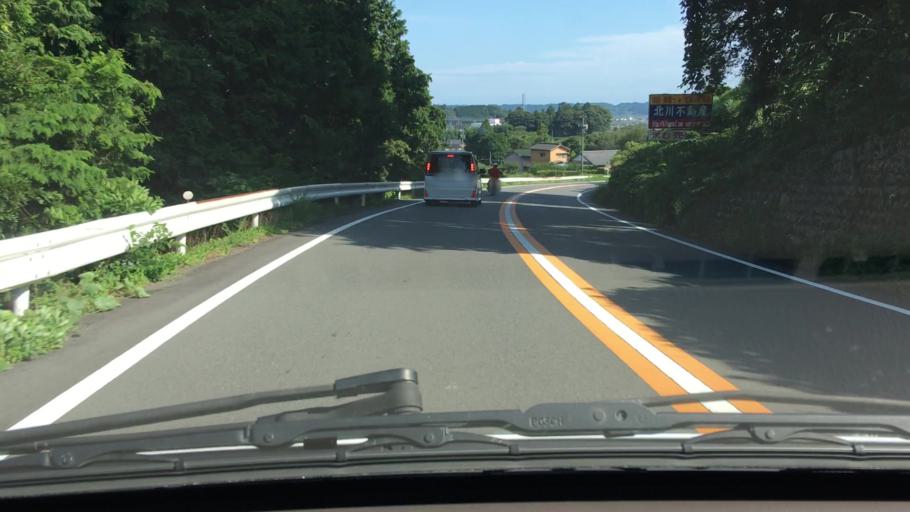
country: JP
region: Shizuoka
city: Kanaya
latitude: 34.8615
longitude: 138.1114
